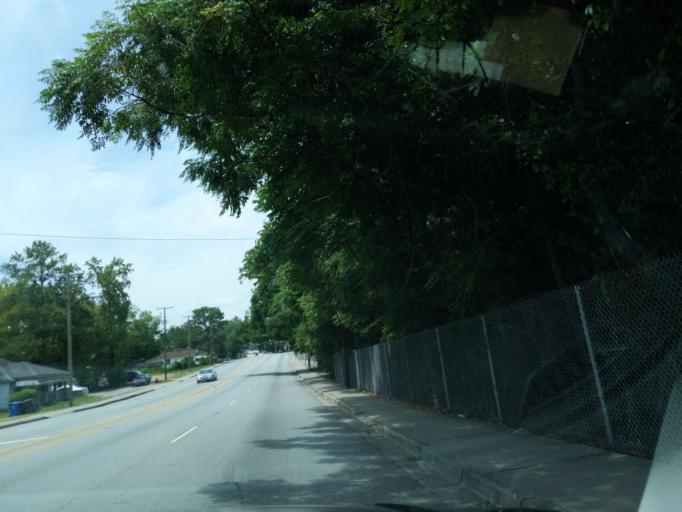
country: US
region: South Carolina
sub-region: Richland County
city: Forest Acres
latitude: 34.0342
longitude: -81.0175
